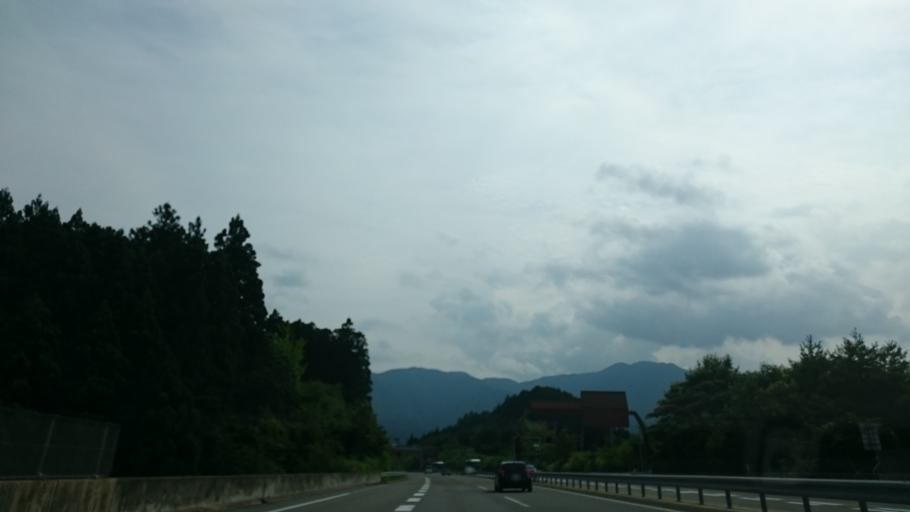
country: JP
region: Gifu
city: Gujo
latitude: 35.8710
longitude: 136.8739
